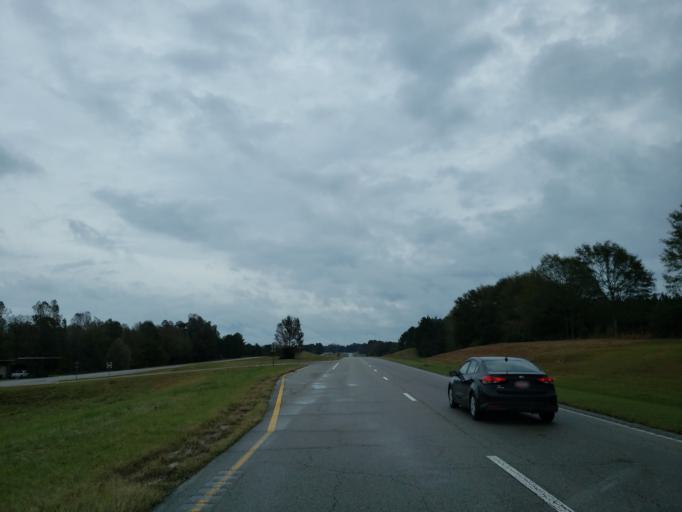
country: US
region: Mississippi
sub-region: Jones County
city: Sharon
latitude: 31.7020
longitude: -88.9081
